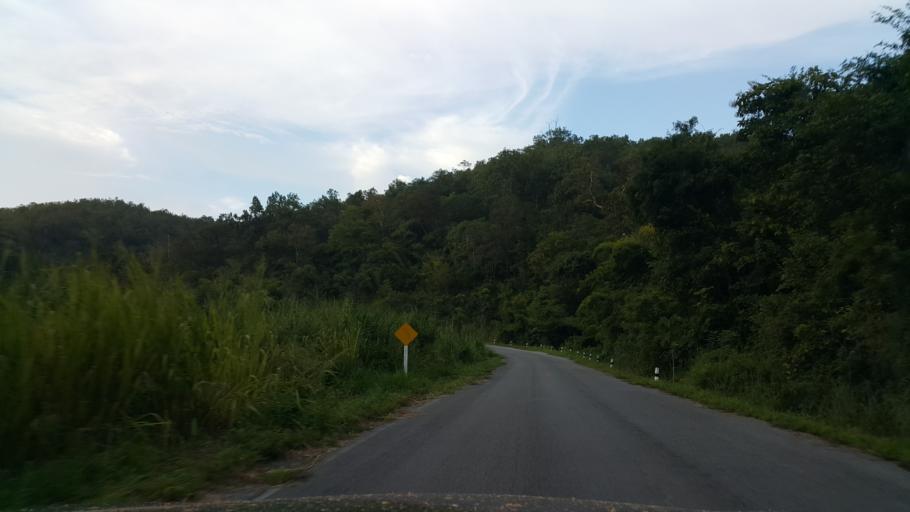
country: TH
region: Mae Hong Son
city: Mae Hi
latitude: 19.2085
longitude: 98.4328
